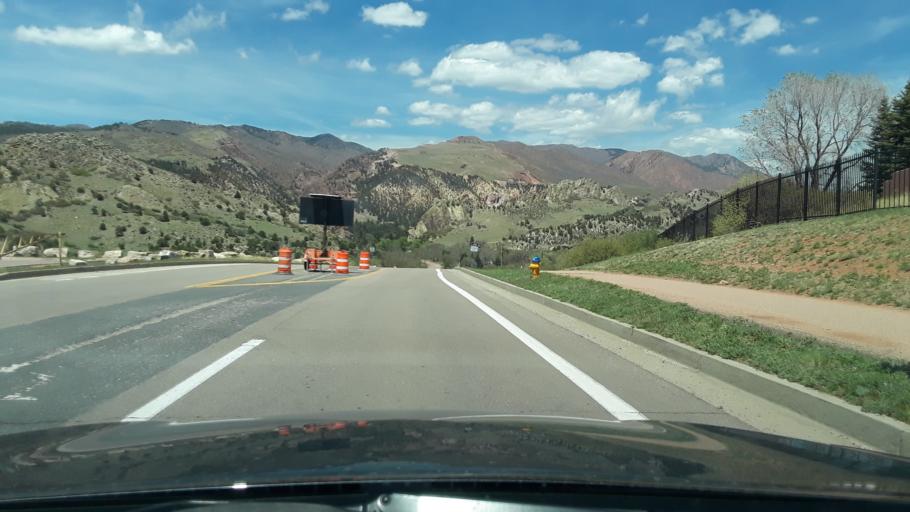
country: US
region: Colorado
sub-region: El Paso County
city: Manitou Springs
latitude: 38.8836
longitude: -104.8723
